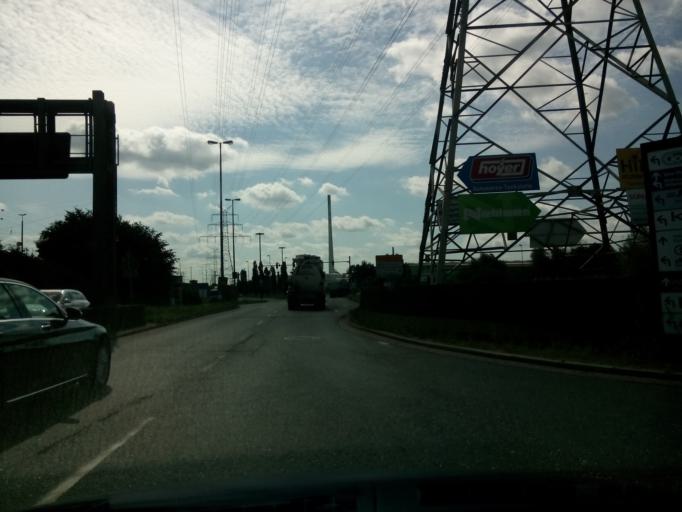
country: DE
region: Lower Saxony
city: Ritterhude
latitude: 53.1354
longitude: 8.7152
